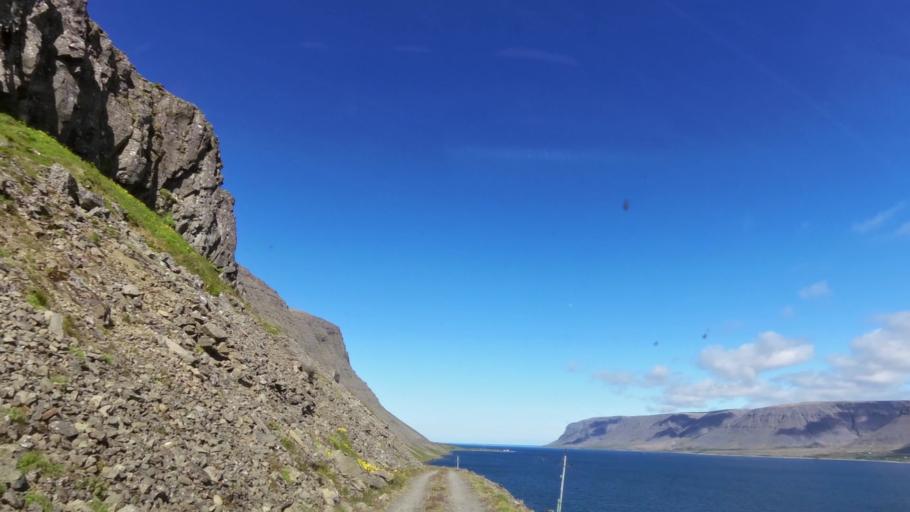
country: IS
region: West
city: Olafsvik
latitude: 65.6239
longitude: -23.8868
